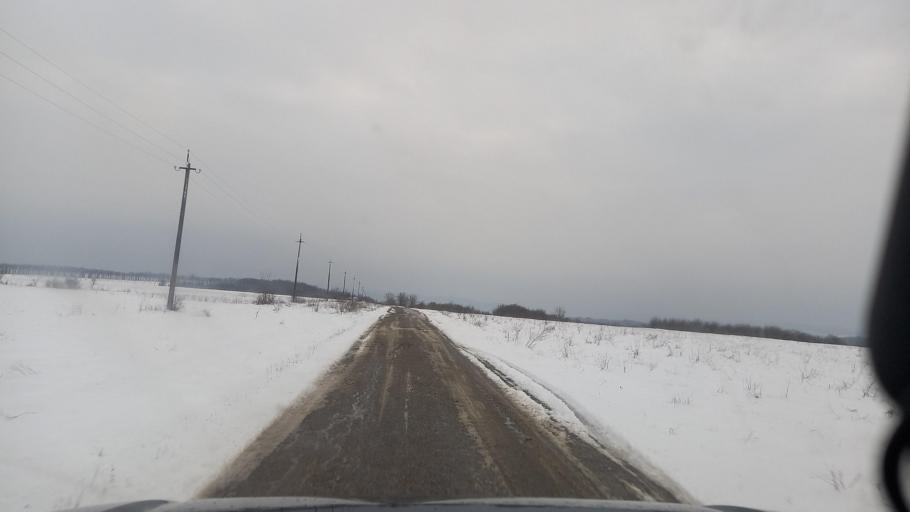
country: RU
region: Krasnodarskiy
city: Novodmitriyevskaya
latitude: 44.8051
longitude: 38.8810
